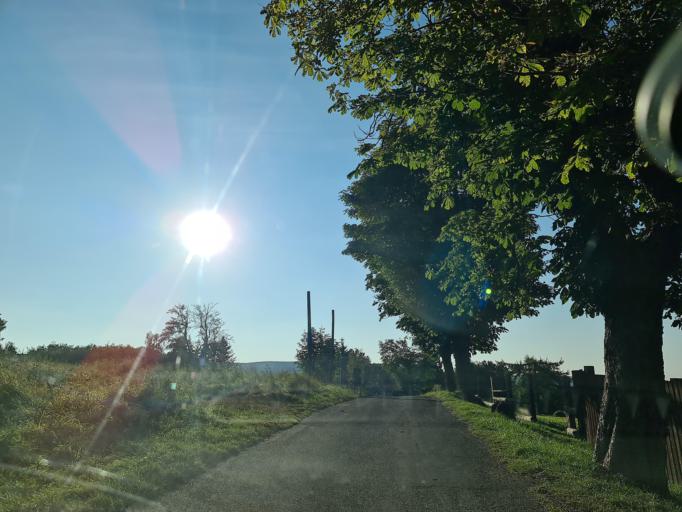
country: DE
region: Saxony
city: Deutschneudorf
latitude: 50.6039
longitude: 13.4426
